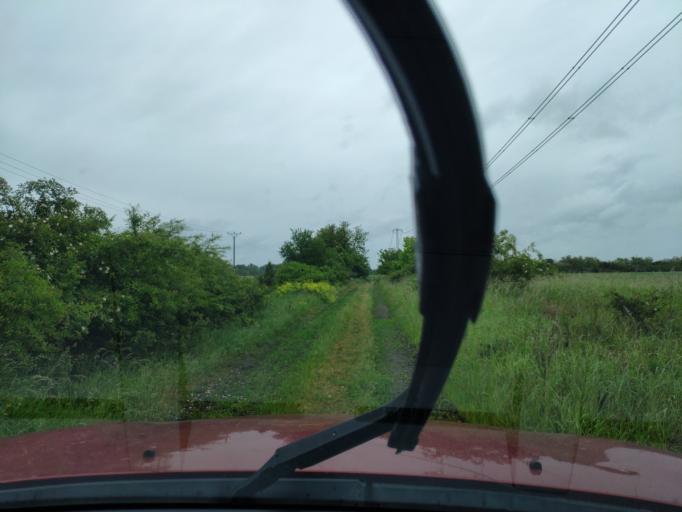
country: SK
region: Kosicky
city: Cierna nad Tisou
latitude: 48.4235
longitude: 22.0634
